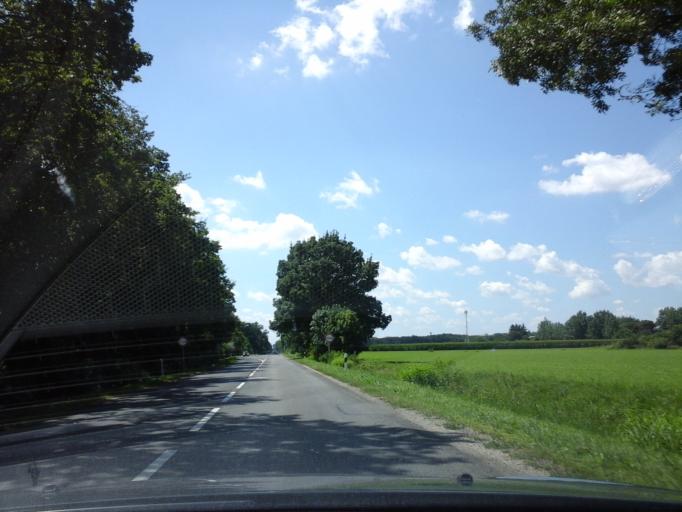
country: HU
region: Hajdu-Bihar
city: Hajduszoboszlo
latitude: 47.4577
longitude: 21.4296
